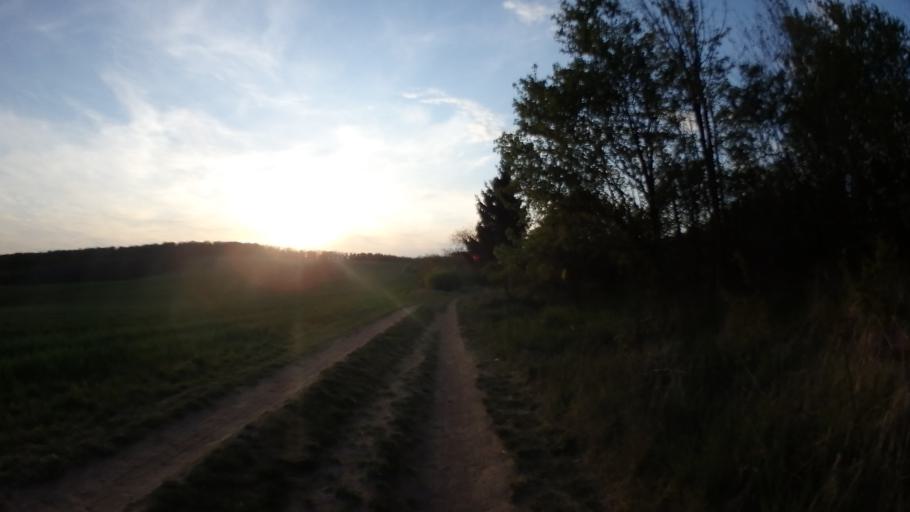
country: CZ
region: South Moravian
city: Ostopovice
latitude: 49.1499
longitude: 16.5439
